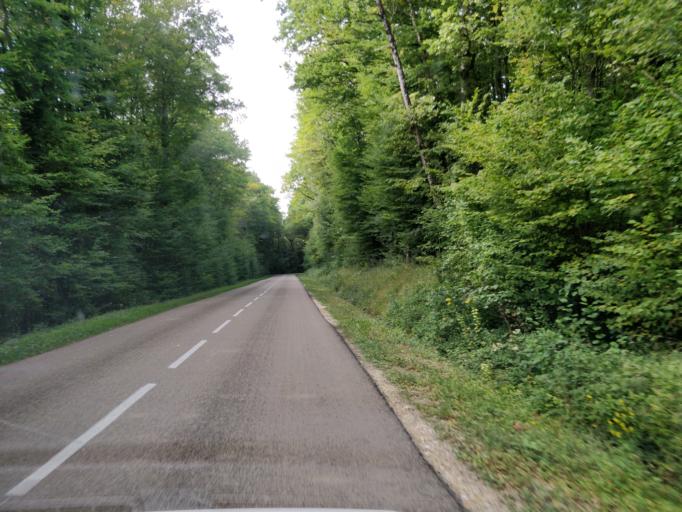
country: FR
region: Champagne-Ardenne
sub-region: Departement de l'Aube
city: Aix-en-Othe
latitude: 48.1394
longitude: 3.6516
